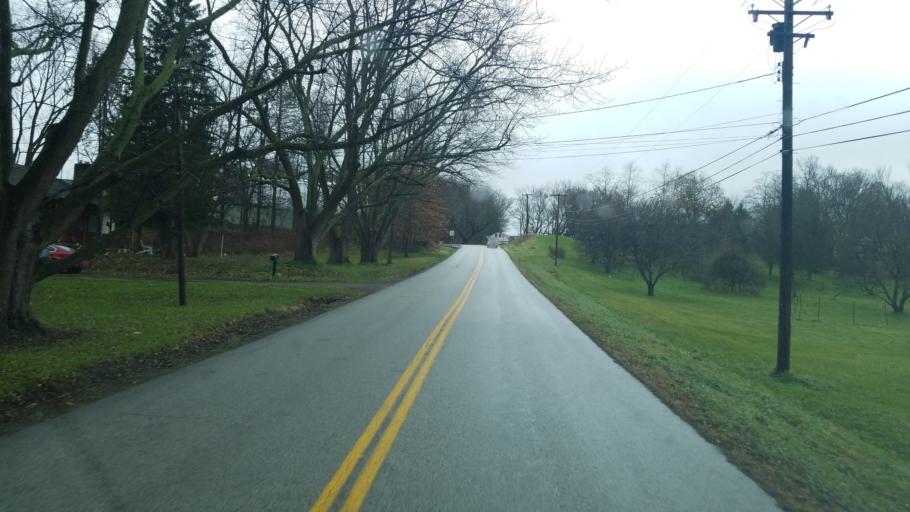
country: US
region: Ohio
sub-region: Ashtabula County
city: Edgewood
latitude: 41.8757
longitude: -80.7323
